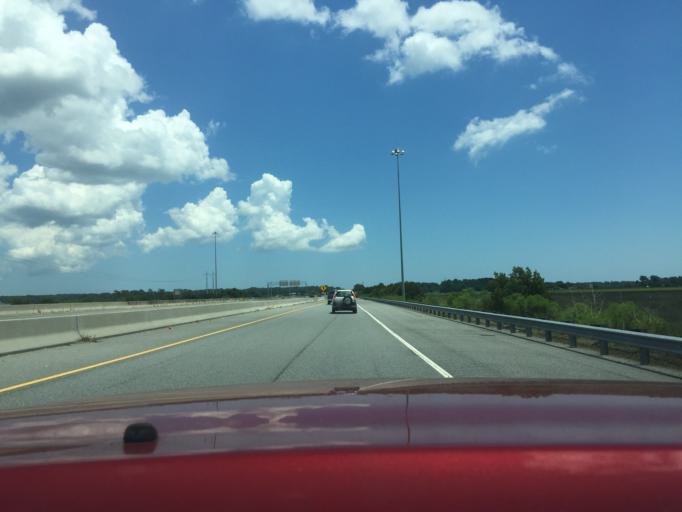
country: US
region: Georgia
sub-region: Chatham County
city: Georgetown
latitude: 31.9841
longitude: -81.1987
